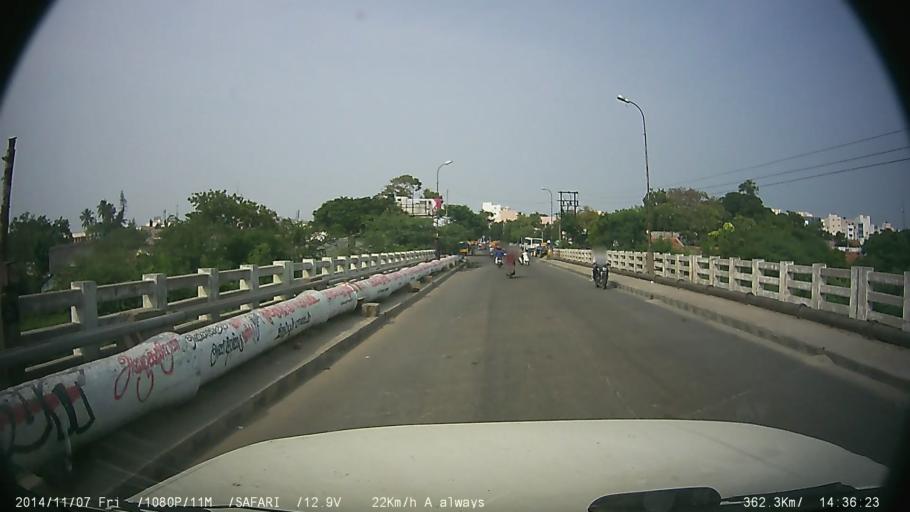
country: IN
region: Tamil Nadu
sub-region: Tiruppur
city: Tiruppur
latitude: 11.1027
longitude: 77.3407
